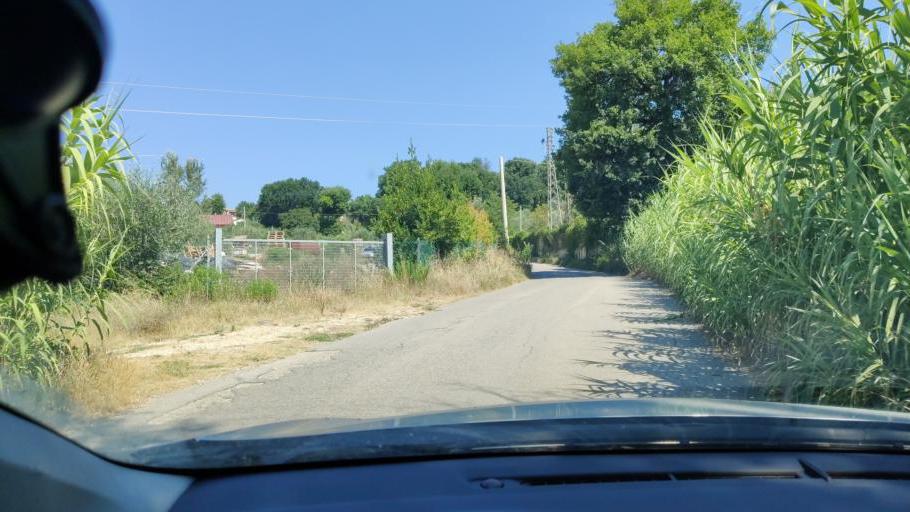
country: IT
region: Umbria
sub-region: Provincia di Terni
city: Amelia
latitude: 42.5467
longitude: 12.4249
